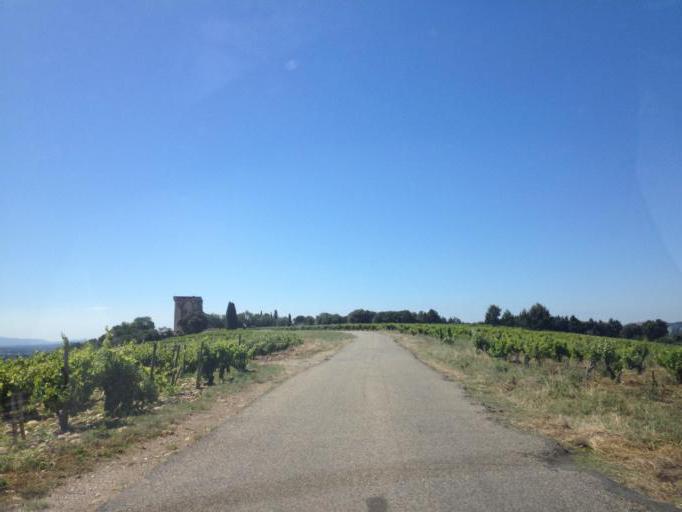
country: FR
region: Provence-Alpes-Cote d'Azur
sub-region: Departement du Vaucluse
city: Chateauneuf-du-Pape
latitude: 44.0609
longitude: 4.8272
